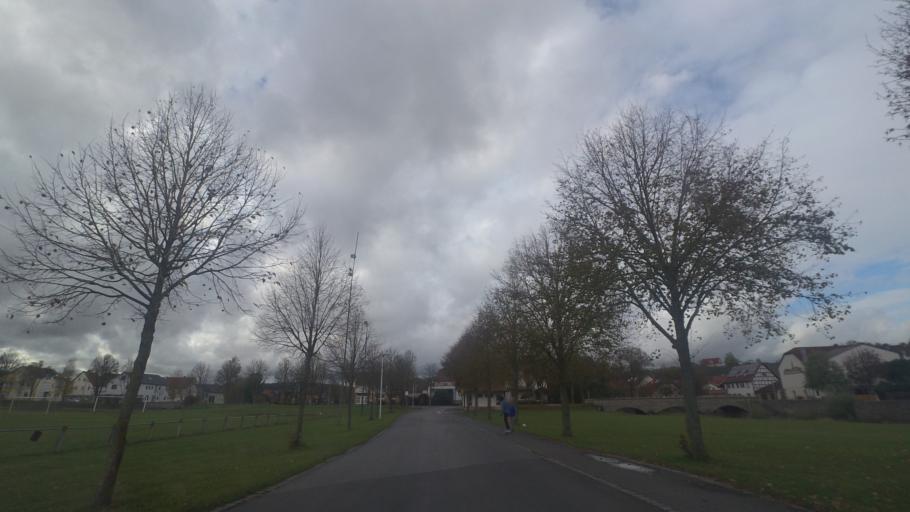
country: DE
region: Bavaria
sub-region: Regierungsbezirk Unterfranken
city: Wuelfershausen
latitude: 50.3307
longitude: 10.3404
